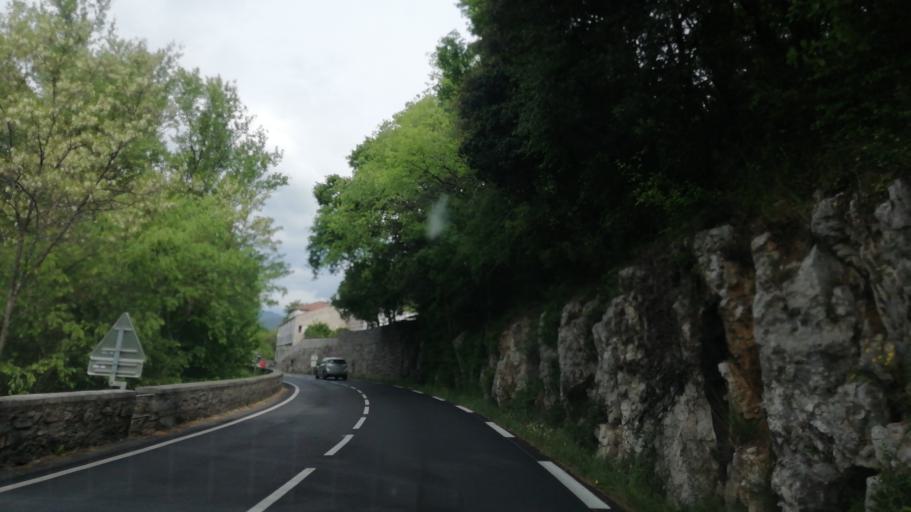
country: FR
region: Languedoc-Roussillon
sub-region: Departement de l'Herault
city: Laroque
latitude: 43.9181
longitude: 3.7277
